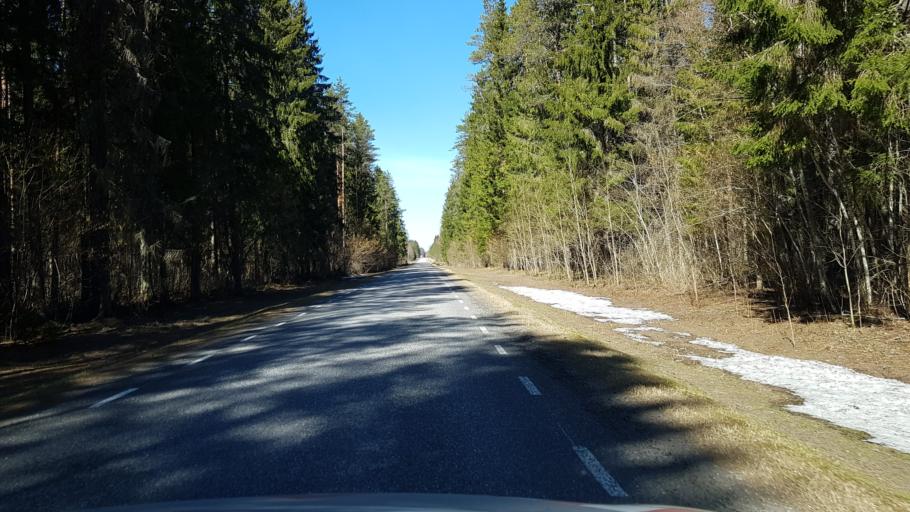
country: EE
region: Laeaene-Virumaa
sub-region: Vinni vald
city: Vinni
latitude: 59.1532
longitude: 26.5172
